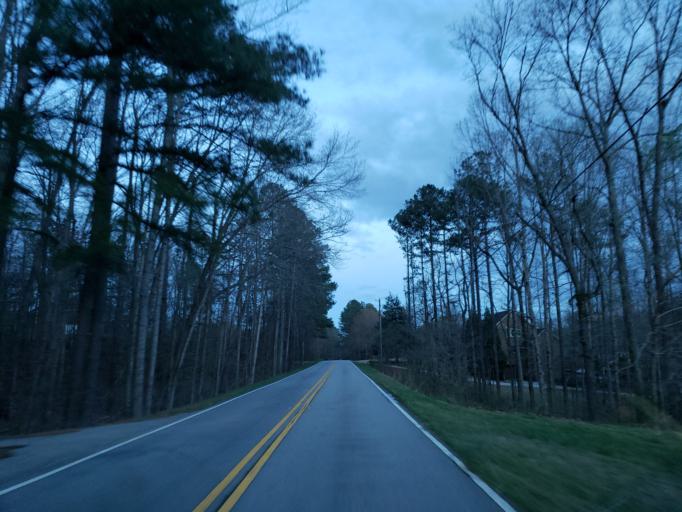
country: US
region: Georgia
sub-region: Paulding County
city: Dallas
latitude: 34.0068
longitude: -84.9059
